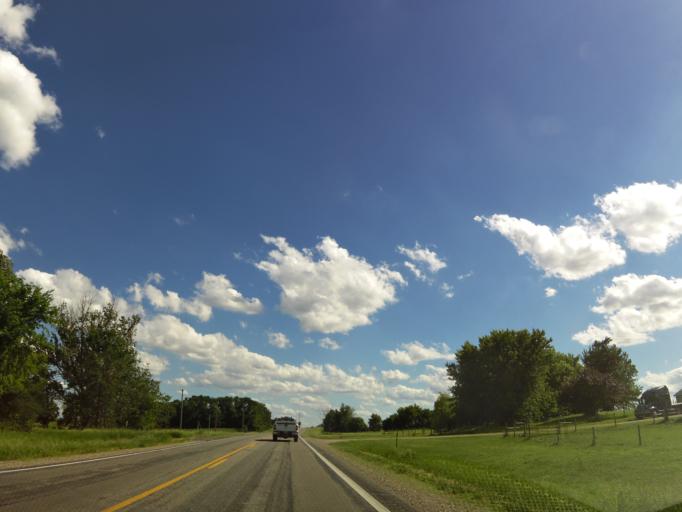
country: US
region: Minnesota
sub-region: Meeker County
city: Dassel
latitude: 45.1907
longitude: -94.3170
